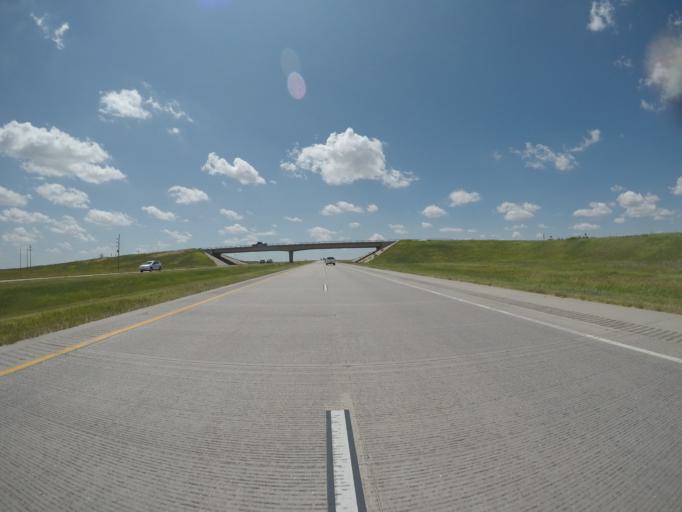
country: US
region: Colorado
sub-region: Lincoln County
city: Hugo
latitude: 39.2843
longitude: -102.9305
